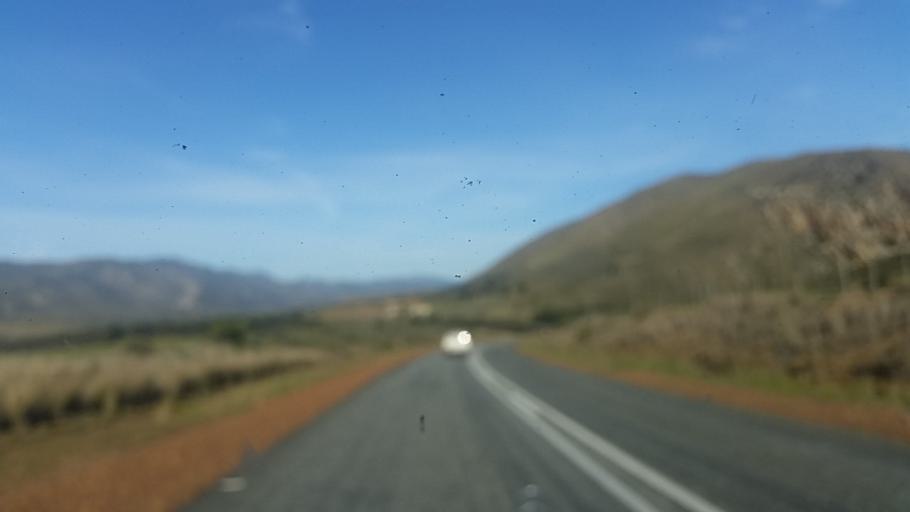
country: ZA
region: Western Cape
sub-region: Eden District Municipality
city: Knysna
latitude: -33.7724
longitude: 22.9485
